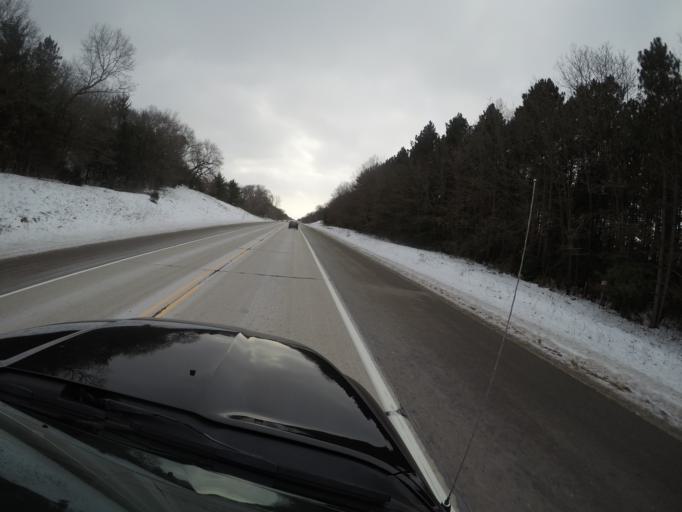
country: US
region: Wisconsin
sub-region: Trempealeau County
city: Galesville
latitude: 44.0548
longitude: -91.2912
